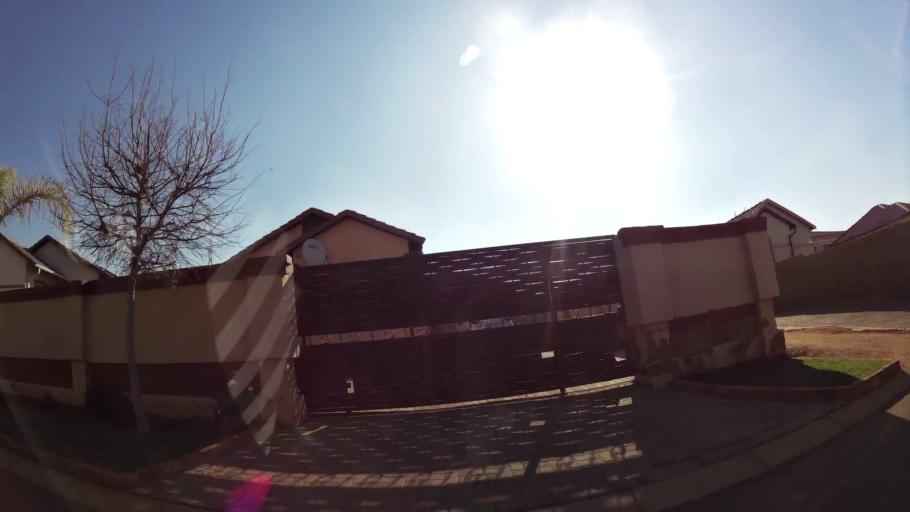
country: ZA
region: Gauteng
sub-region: West Rand District Municipality
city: Muldersdriseloop
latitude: -26.0323
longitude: 27.9153
